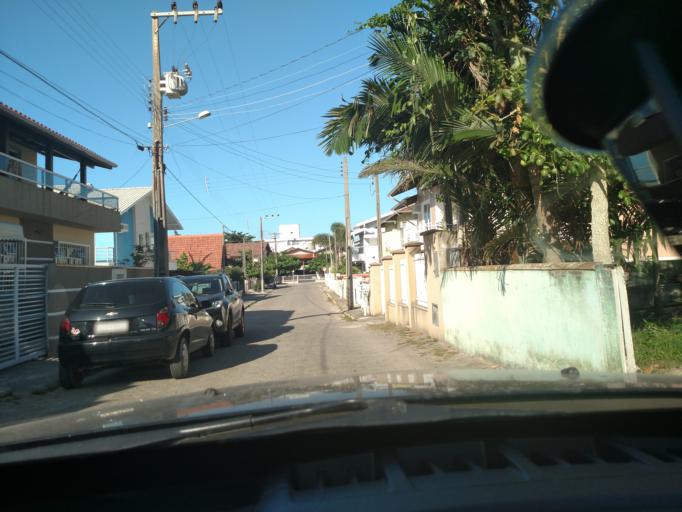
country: BR
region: Santa Catarina
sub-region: Porto Belo
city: Porto Belo
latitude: -27.1992
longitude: -48.4984
